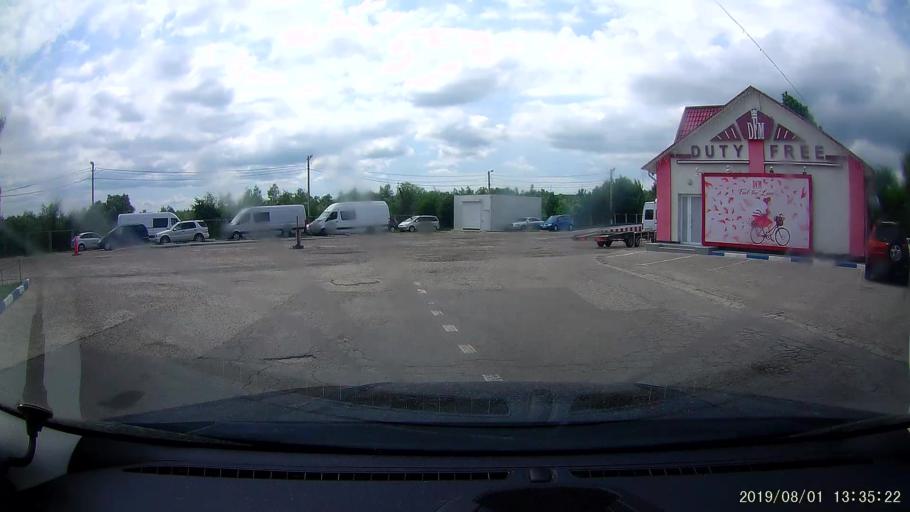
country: RO
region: Galati
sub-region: Comuna Oancea
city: Oancea
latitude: 45.9166
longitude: 28.1255
